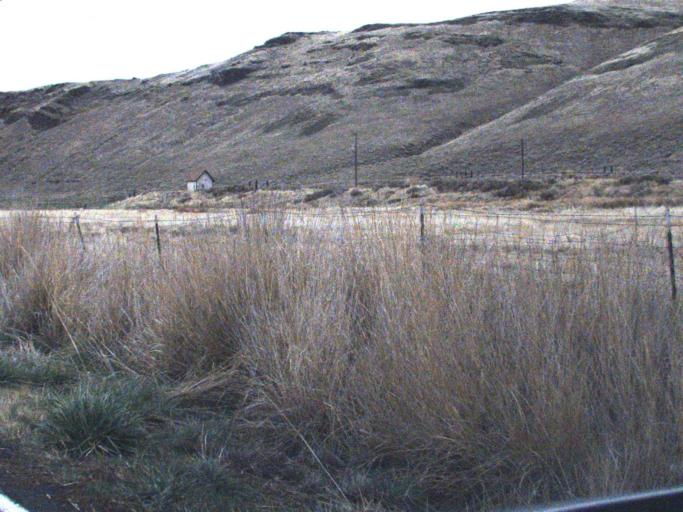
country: US
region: Washington
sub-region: Walla Walla County
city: Waitsburg
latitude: 46.5229
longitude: -118.1303
